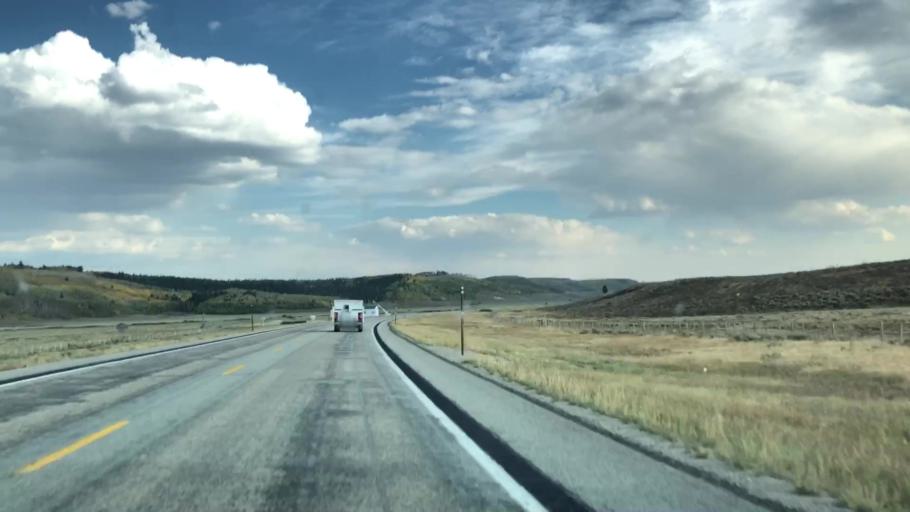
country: US
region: Wyoming
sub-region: Sublette County
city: Pinedale
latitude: 43.1183
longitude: -110.1788
